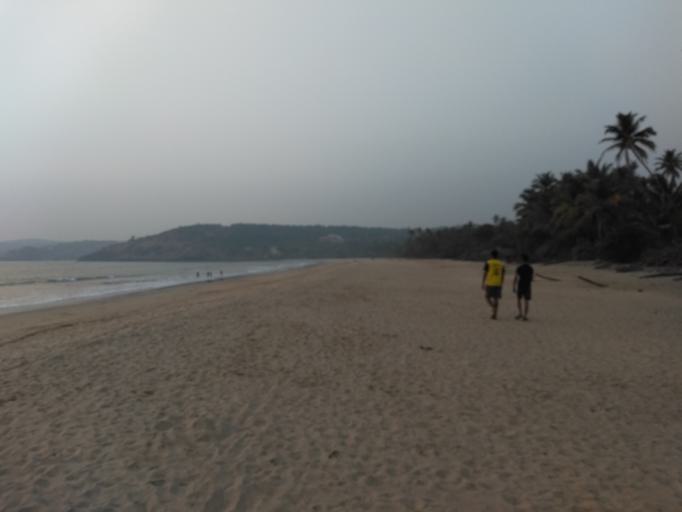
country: IN
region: Maharashtra
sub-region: Ratnagiri
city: Guhagar
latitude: 17.3791
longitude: 73.2094
